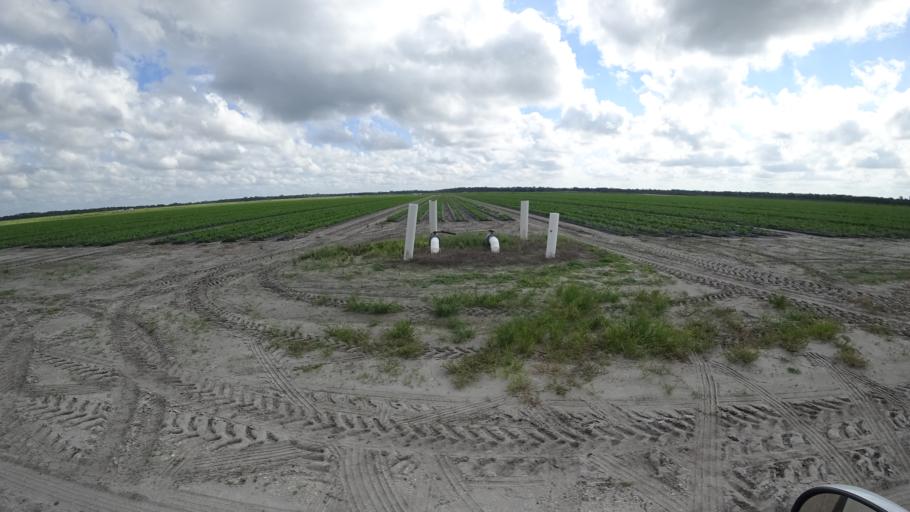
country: US
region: Florida
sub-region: Sarasota County
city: Lake Sarasota
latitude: 27.4056
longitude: -82.2117
